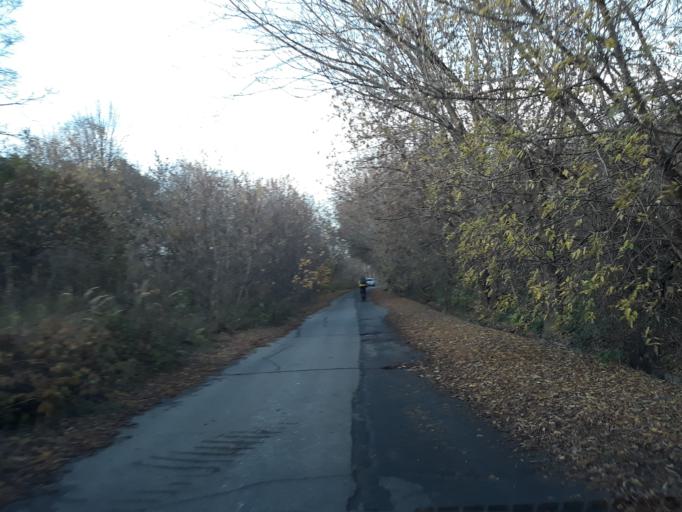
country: RU
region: Nizjnij Novgorod
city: Nizhniy Novgorod
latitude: 56.2803
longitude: 43.9696
